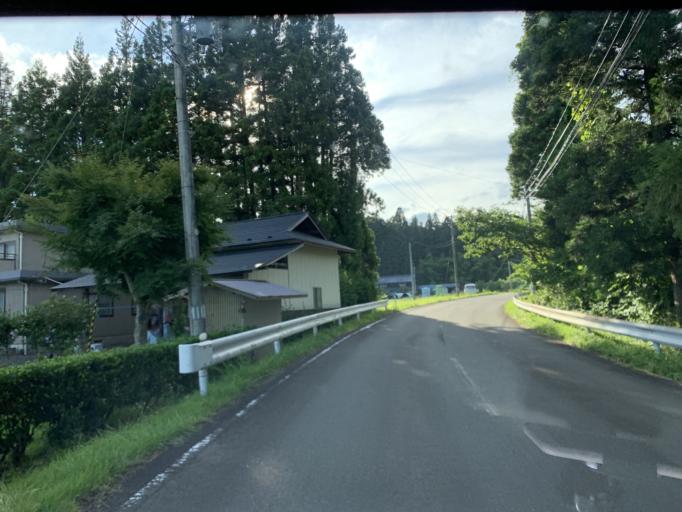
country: JP
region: Iwate
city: Ichinoseki
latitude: 38.8985
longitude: 140.9350
